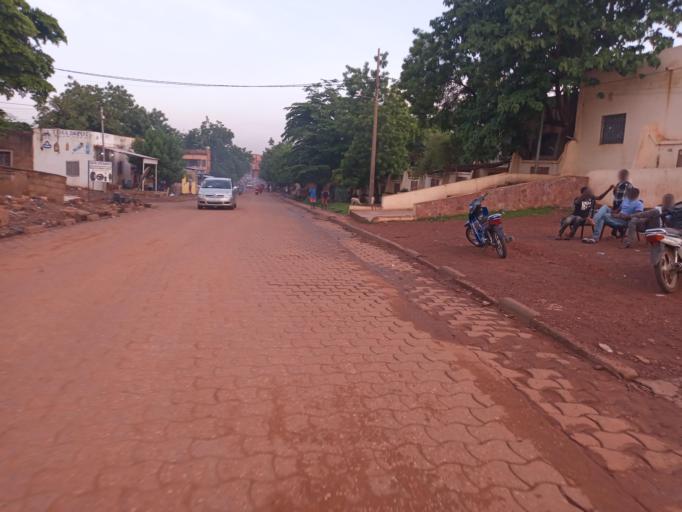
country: ML
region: Bamako
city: Bamako
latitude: 12.6433
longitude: -8.0312
